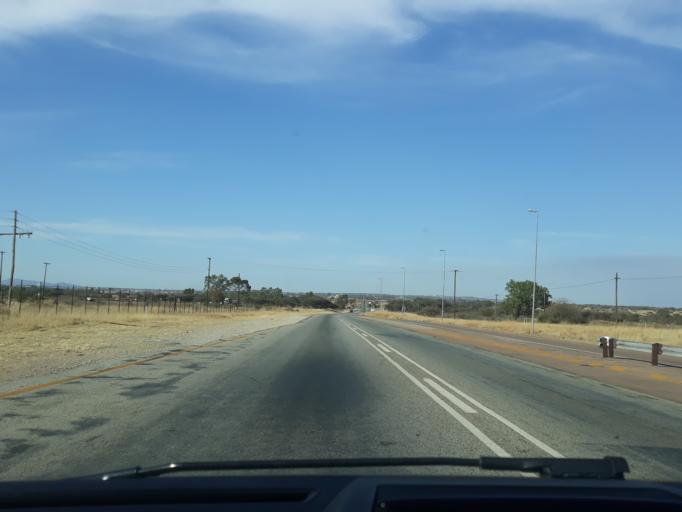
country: ZA
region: Limpopo
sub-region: Capricorn District Municipality
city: Polokwane
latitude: -23.9522
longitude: 29.3983
